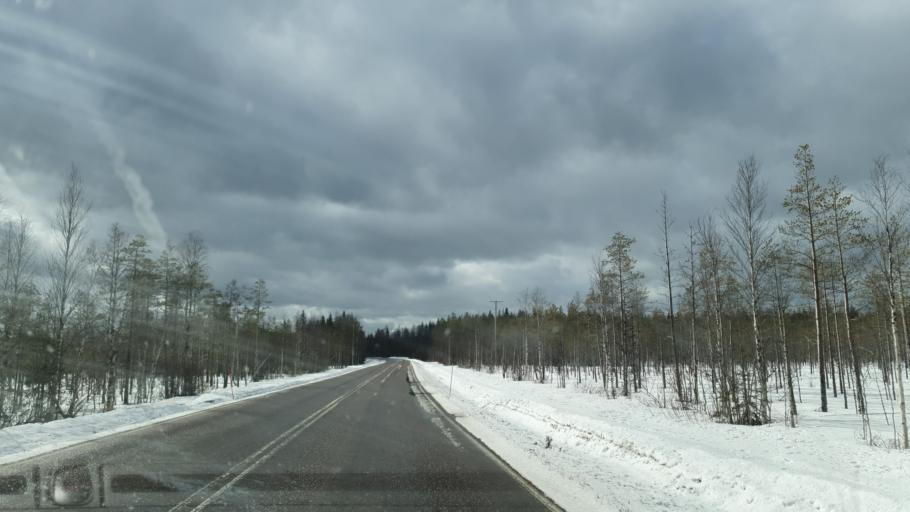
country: FI
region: Kainuu
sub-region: Kehys-Kainuu
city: Puolanka
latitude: 65.0233
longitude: 27.6987
